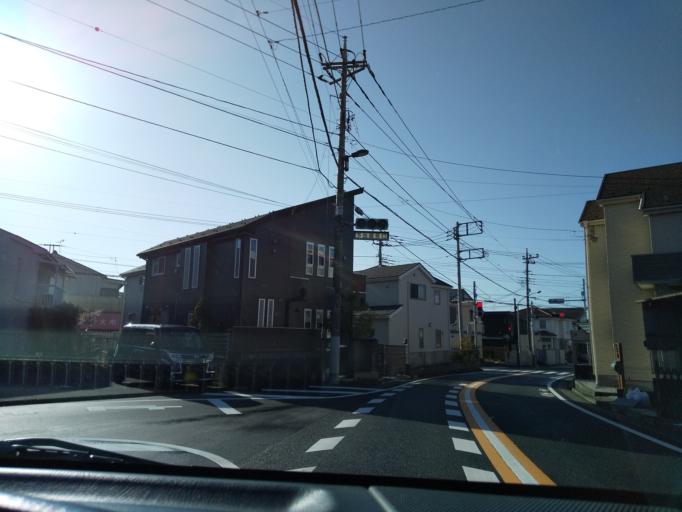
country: JP
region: Tokyo
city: Hino
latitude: 35.6907
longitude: 139.4128
